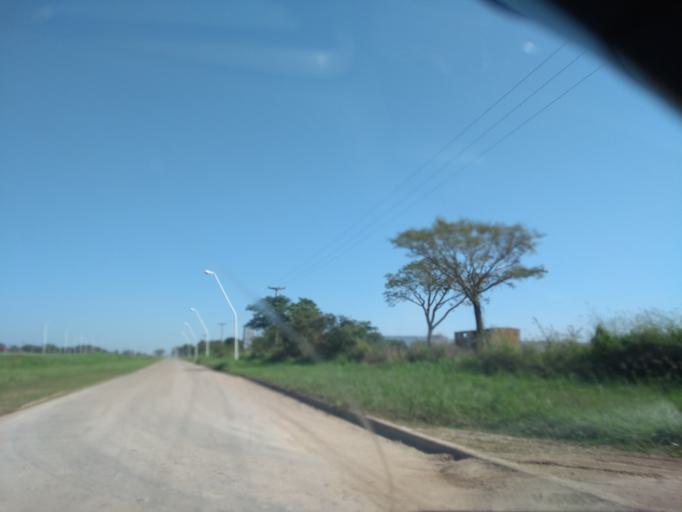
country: AR
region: Chaco
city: Barranqueras
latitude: -27.4314
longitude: -58.9298
